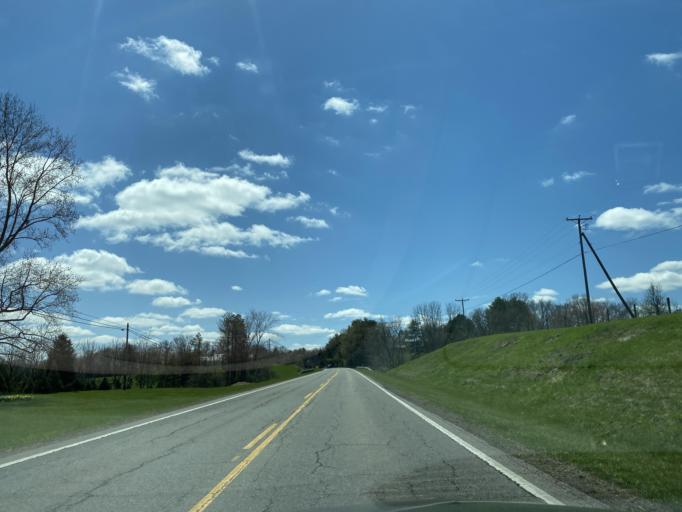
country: US
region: Ohio
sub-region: Wayne County
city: Shreve
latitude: 40.6939
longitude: -82.0211
